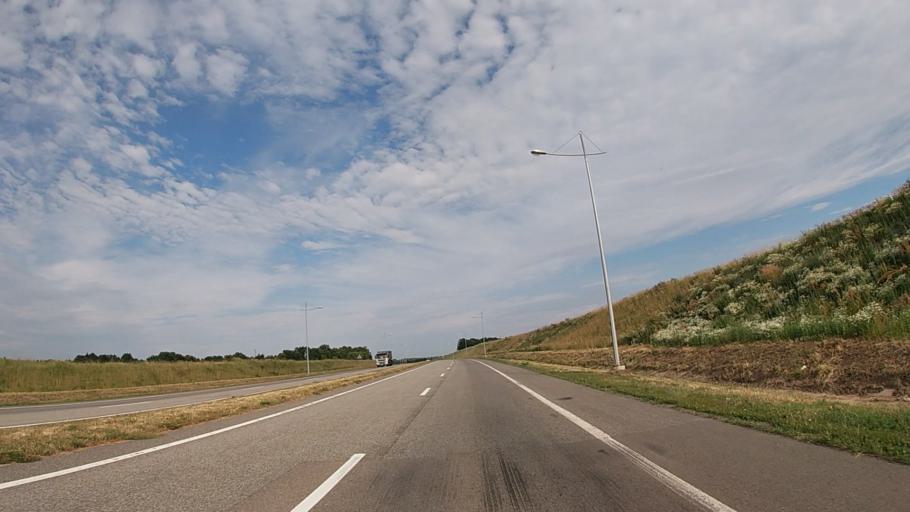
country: RU
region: Belgorod
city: Tomarovka
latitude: 50.7052
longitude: 36.2175
